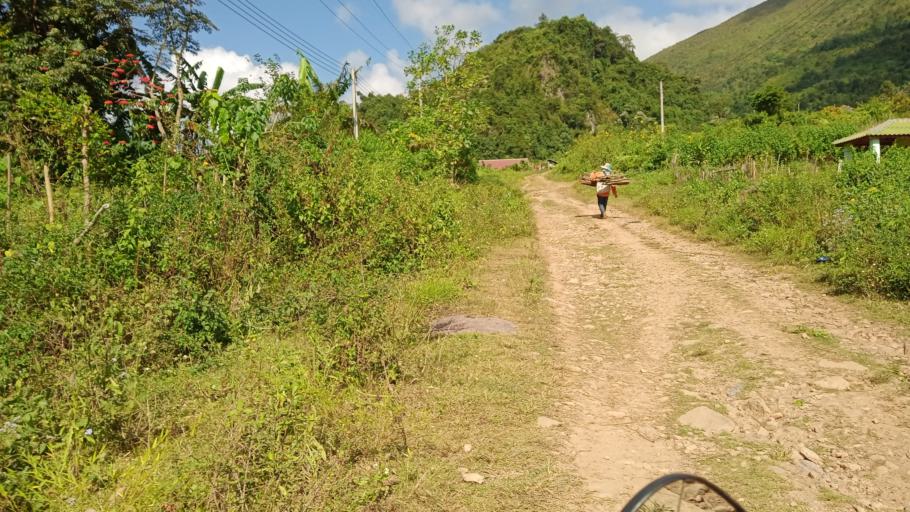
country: LA
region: Xiangkhoang
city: Phonsavan
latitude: 19.1117
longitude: 102.9256
